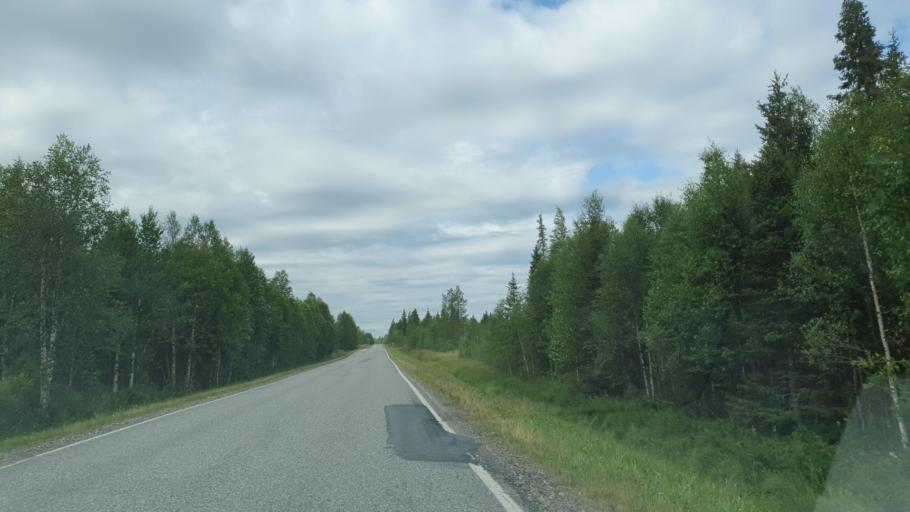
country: FI
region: Lapland
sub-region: Tunturi-Lappi
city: Kittilae
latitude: 67.6156
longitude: 25.3596
